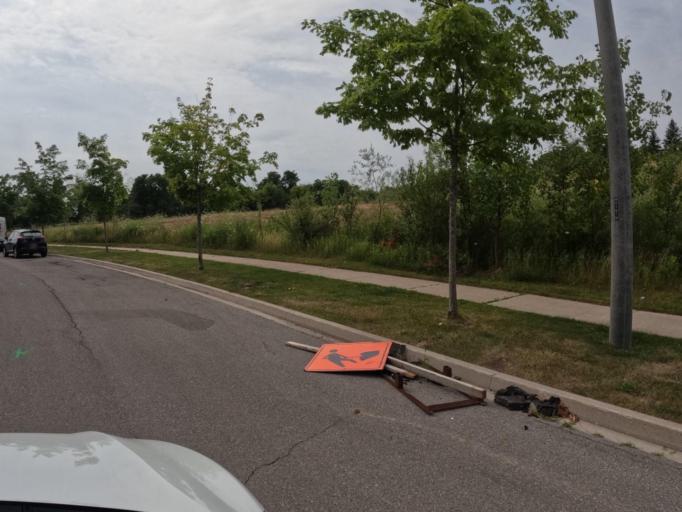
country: CA
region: Ontario
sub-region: Halton
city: Milton
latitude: 43.6423
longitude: -79.9344
